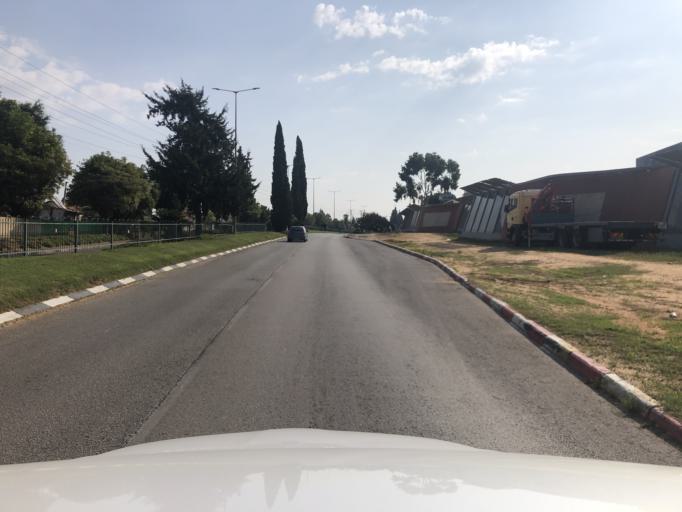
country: IL
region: Central District
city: Kfar Saba
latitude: 32.1903
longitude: 34.8960
